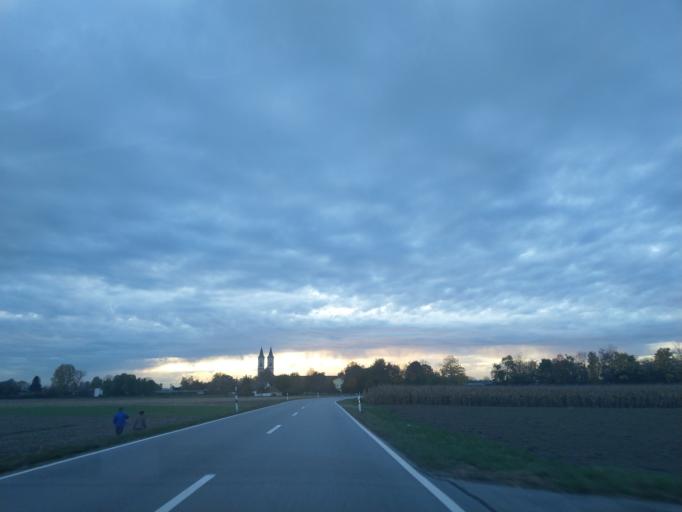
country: DE
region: Bavaria
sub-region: Lower Bavaria
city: Niederalteich
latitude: 48.7642
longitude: 13.0374
